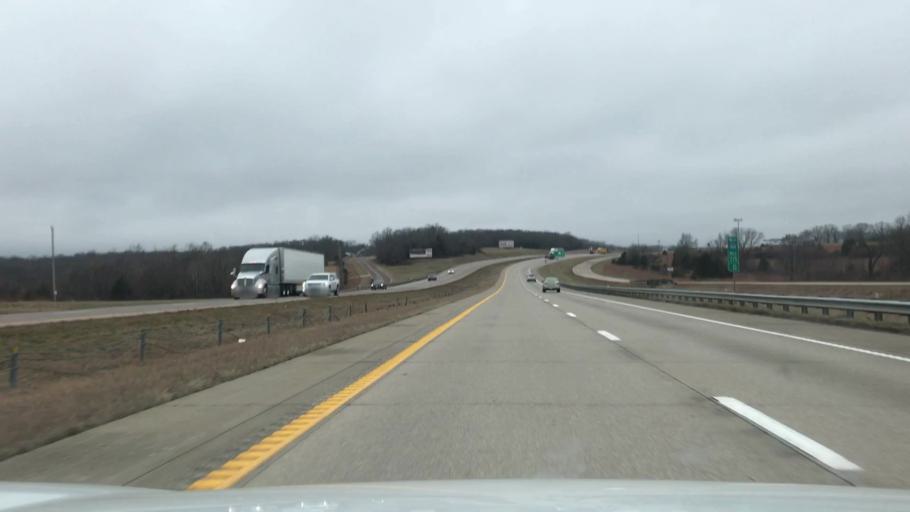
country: US
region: Missouri
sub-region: Crawford County
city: Bourbon
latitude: 38.1250
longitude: -91.3077
